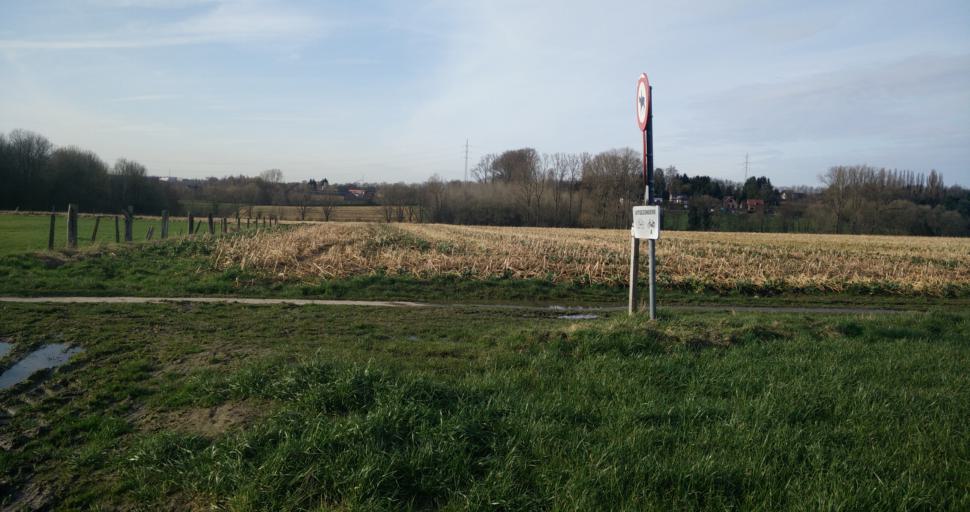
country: BE
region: Flanders
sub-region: Provincie Vlaams-Brabant
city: Halle
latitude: 50.7147
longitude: 4.2484
